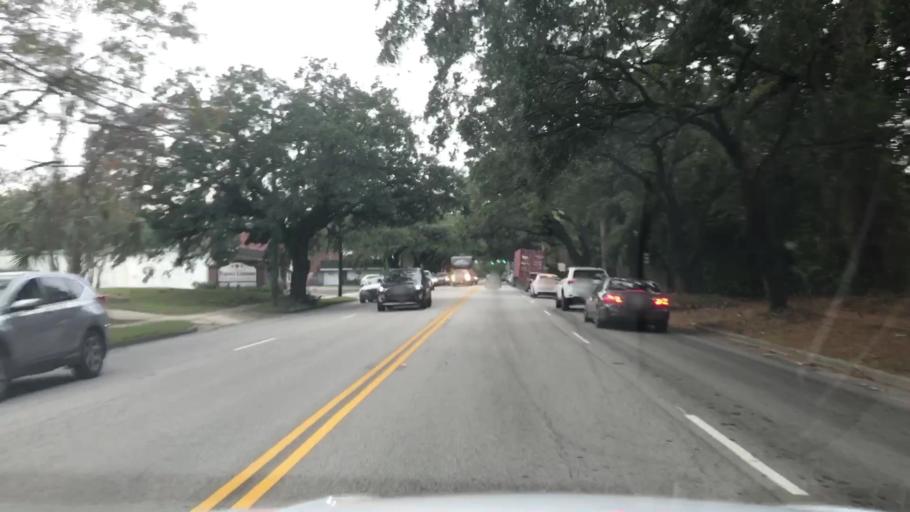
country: US
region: South Carolina
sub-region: Georgetown County
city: Georgetown
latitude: 33.3721
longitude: -79.2808
